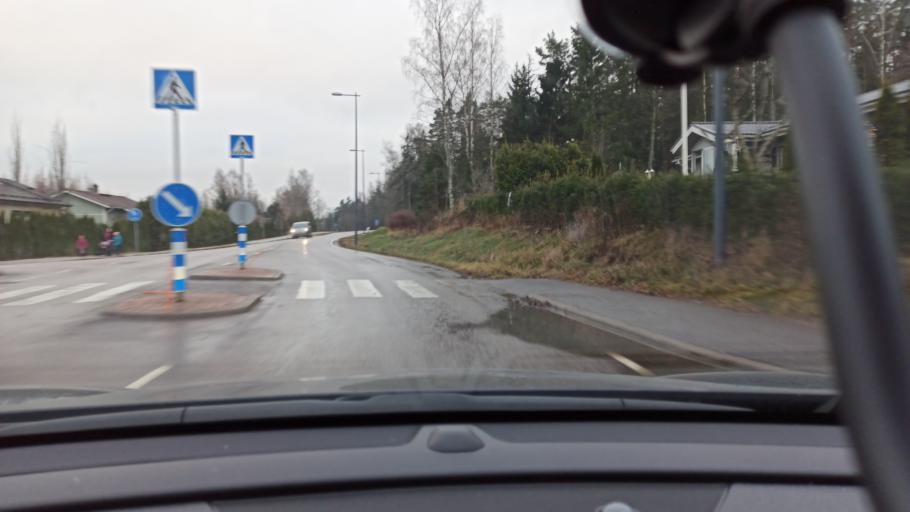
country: FI
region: Uusimaa
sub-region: Helsinki
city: Kirkkonummi
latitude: 60.1245
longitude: 24.4696
